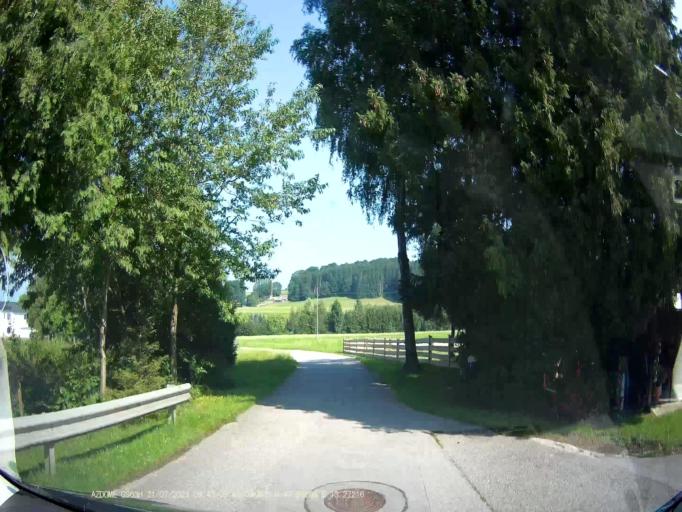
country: AT
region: Salzburg
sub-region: Politischer Bezirk Salzburg-Umgebung
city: Strasswalchen
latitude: 47.9823
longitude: 13.2720
